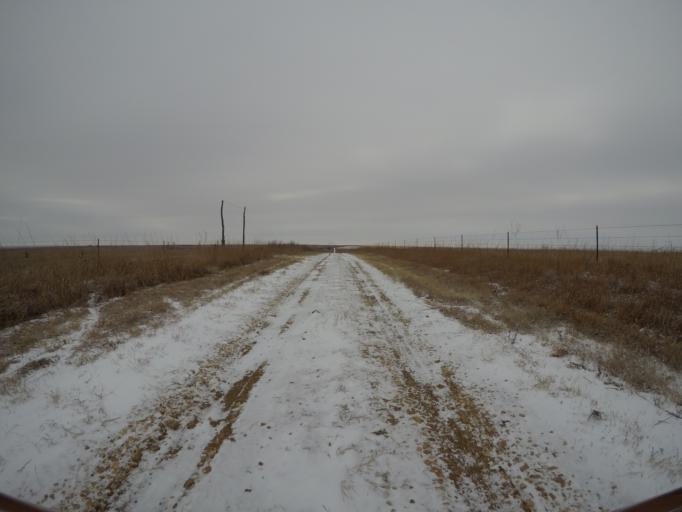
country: US
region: Kansas
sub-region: Wabaunsee County
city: Alma
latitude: 38.8935
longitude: -96.1136
